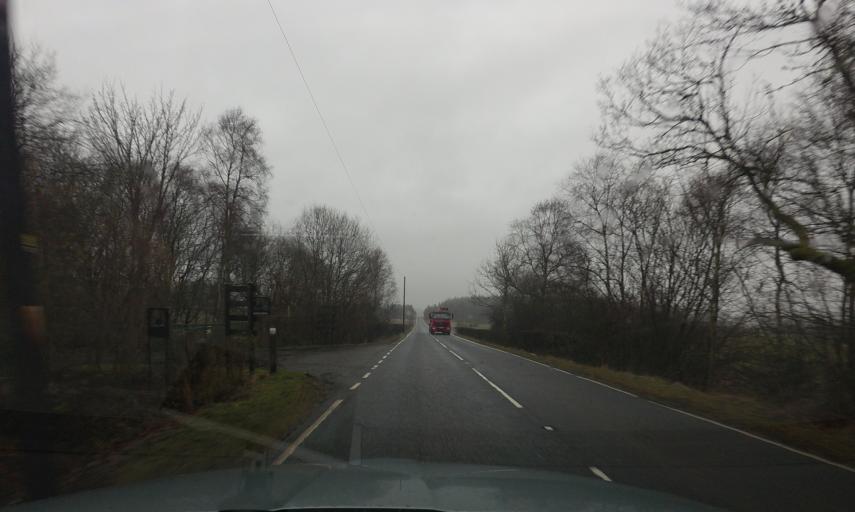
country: GB
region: Scotland
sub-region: Stirling
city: Balfron
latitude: 56.1152
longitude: -4.3589
